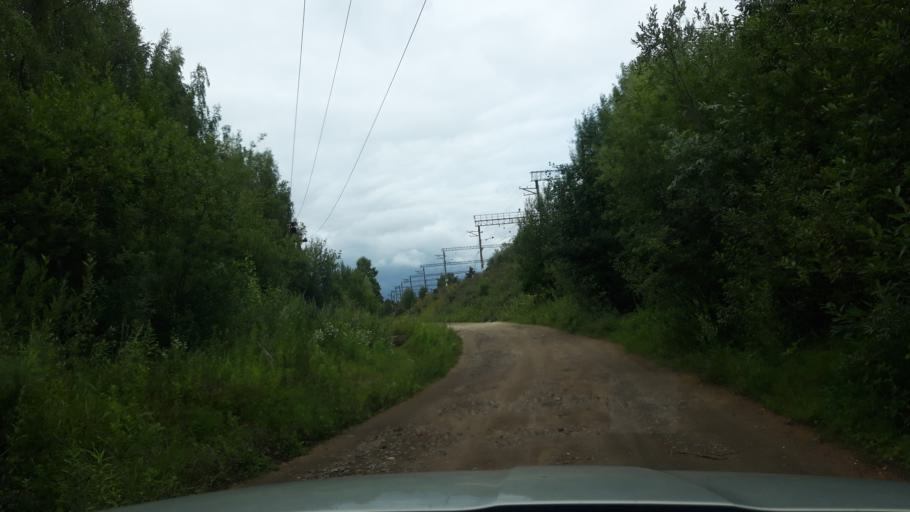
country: RU
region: Moskovskaya
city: Povarovo
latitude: 56.0555
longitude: 37.0582
